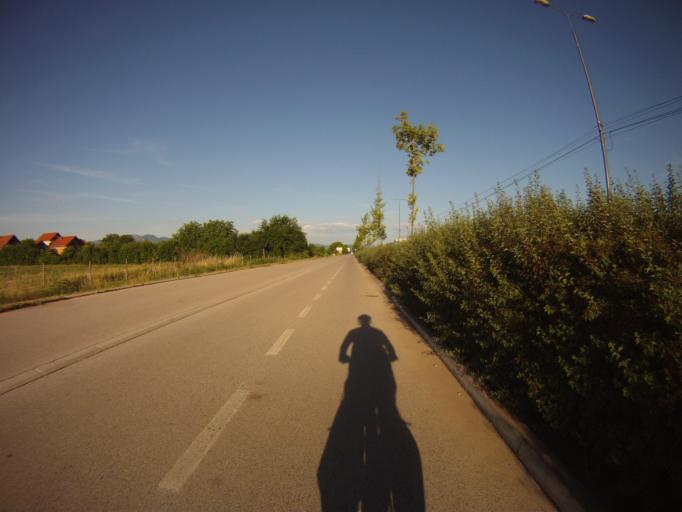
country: RS
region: Central Serbia
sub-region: Nisavski Okrug
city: Niska Banja
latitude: 43.3072
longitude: 21.9551
